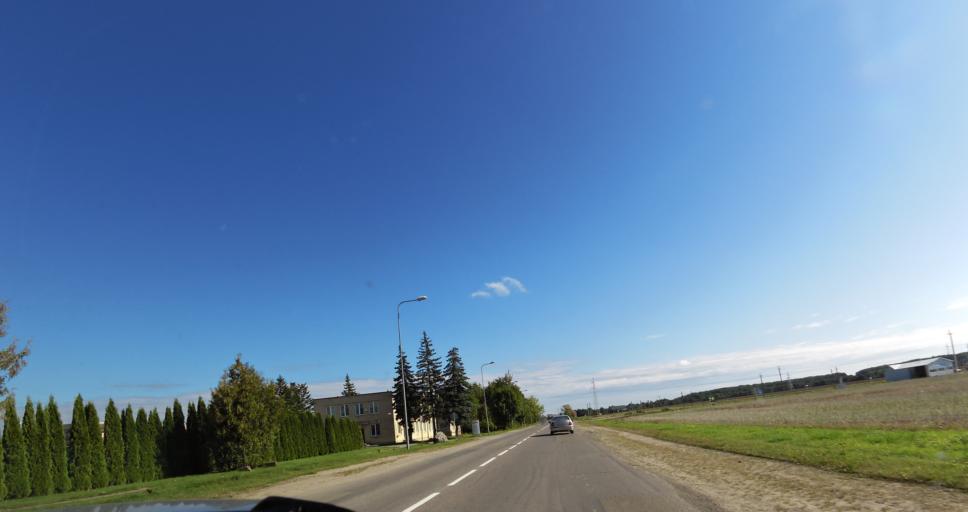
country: LT
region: Panevezys
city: Pasvalys
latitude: 56.0645
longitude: 24.4224
